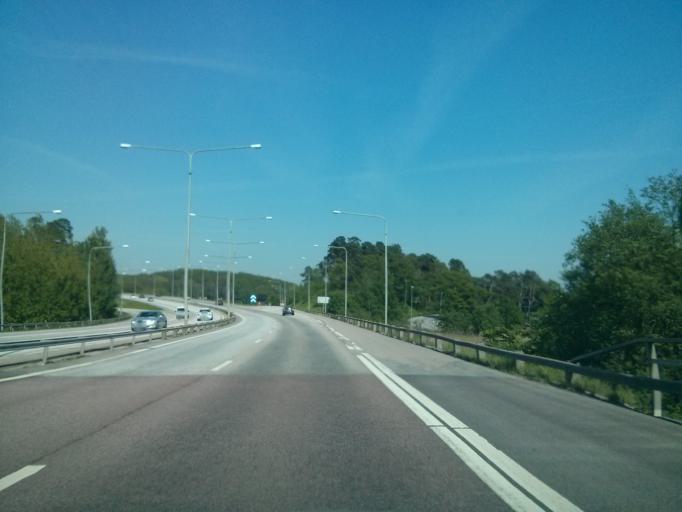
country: SE
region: Blekinge
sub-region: Karlskrona Kommun
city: Karlskrona
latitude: 56.1761
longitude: 15.6034
